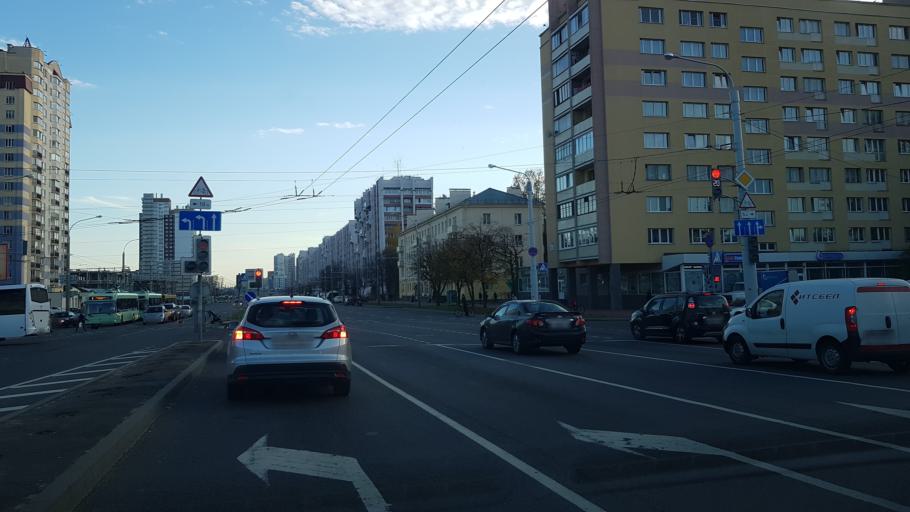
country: BY
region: Minsk
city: Minsk
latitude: 53.8839
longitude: 27.5678
